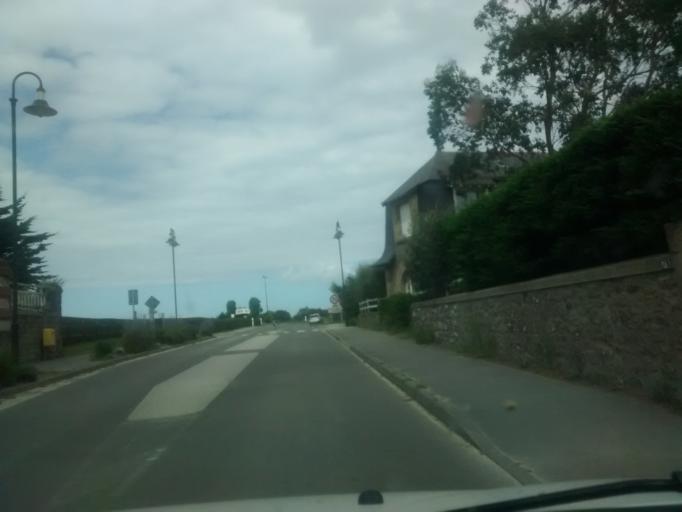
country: FR
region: Brittany
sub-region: Departement d'Ille-et-Vilaine
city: Saint-Briac-sur-Mer
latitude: 48.6314
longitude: -2.1358
